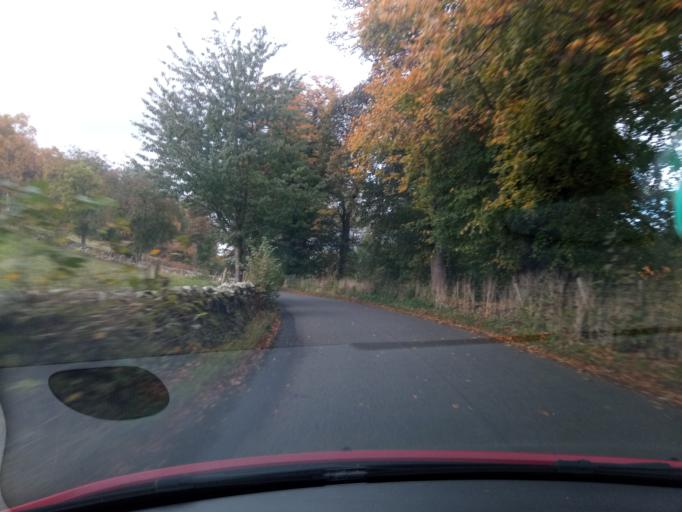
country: GB
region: Scotland
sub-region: The Scottish Borders
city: Peebles
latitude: 55.6401
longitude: -3.1509
